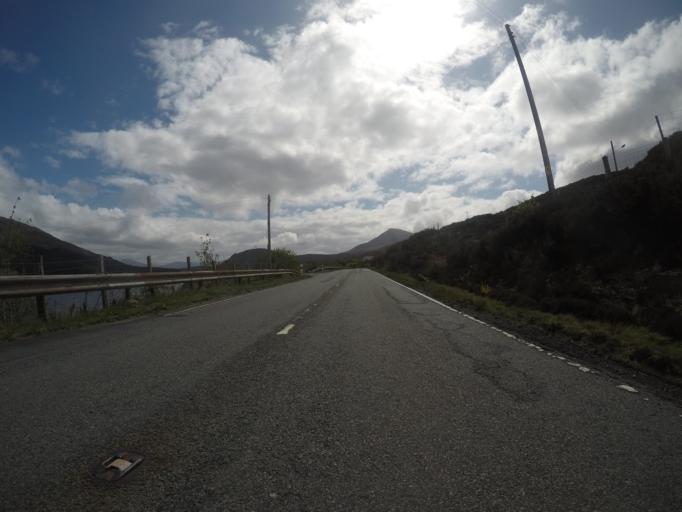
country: GB
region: Scotland
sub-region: Highland
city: Portree
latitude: 57.2828
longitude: -6.0139
